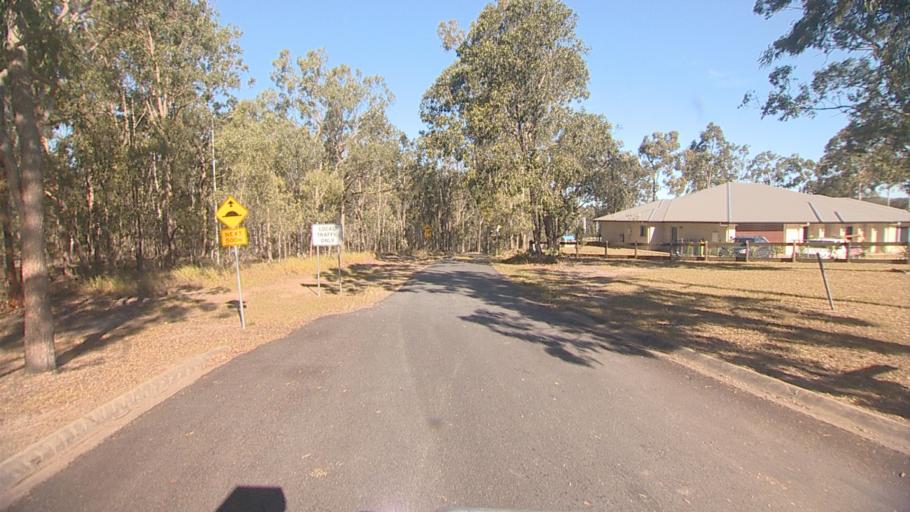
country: AU
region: Queensland
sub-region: Ipswich
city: Springfield Lakes
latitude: -27.7342
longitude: 152.9226
